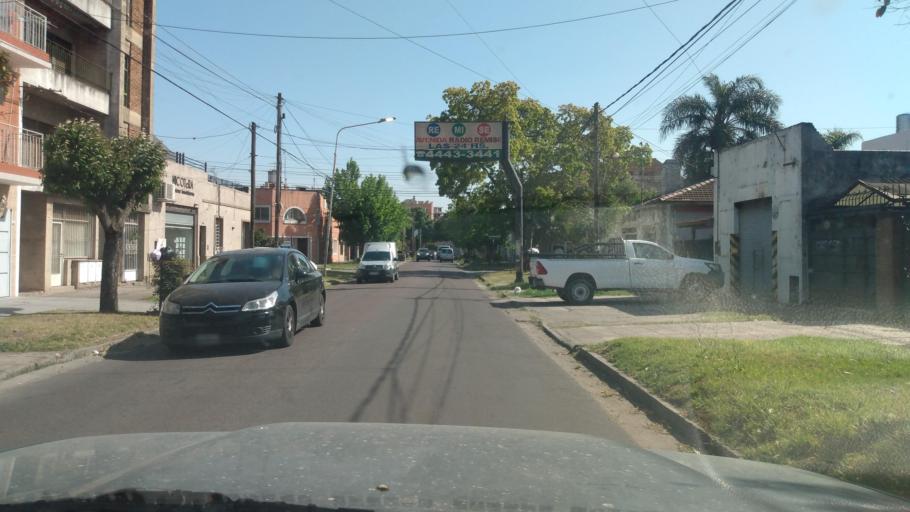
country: AR
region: Buenos Aires
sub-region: Partido de Moron
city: Moron
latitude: -34.6388
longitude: -58.5960
